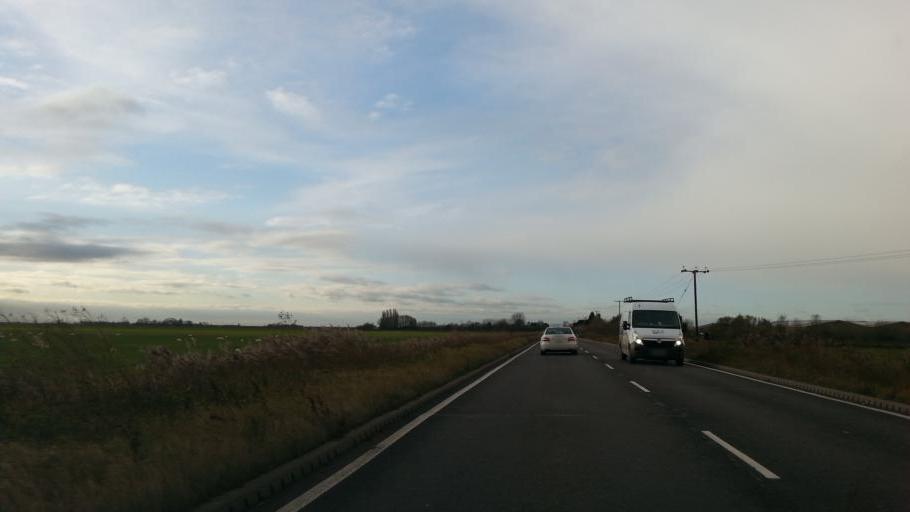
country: GB
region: England
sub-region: Cambridgeshire
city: March
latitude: 52.6110
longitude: 0.0280
